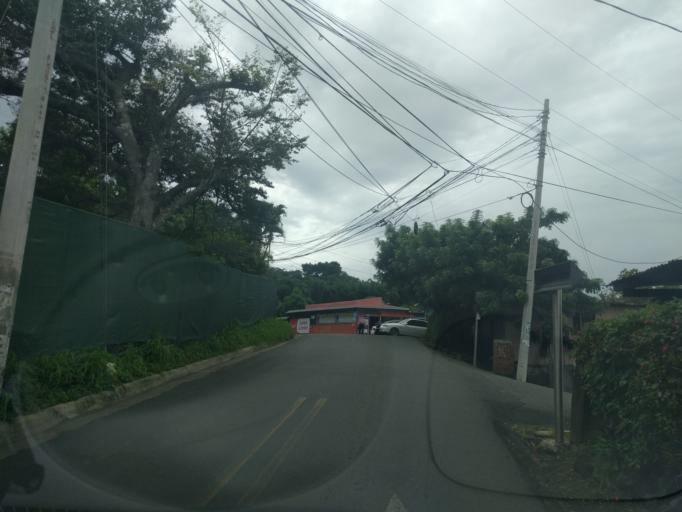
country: CR
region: Heredia
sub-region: Canton de Belen
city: San Antonio
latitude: 9.9612
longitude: -84.1902
